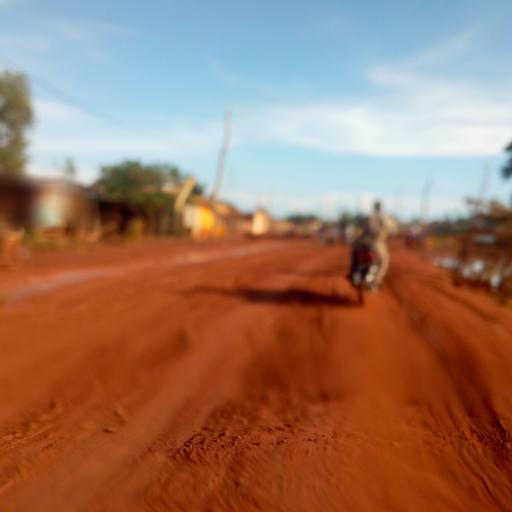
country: BJ
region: Atlantique
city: Hevie
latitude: 6.4199
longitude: 2.2612
